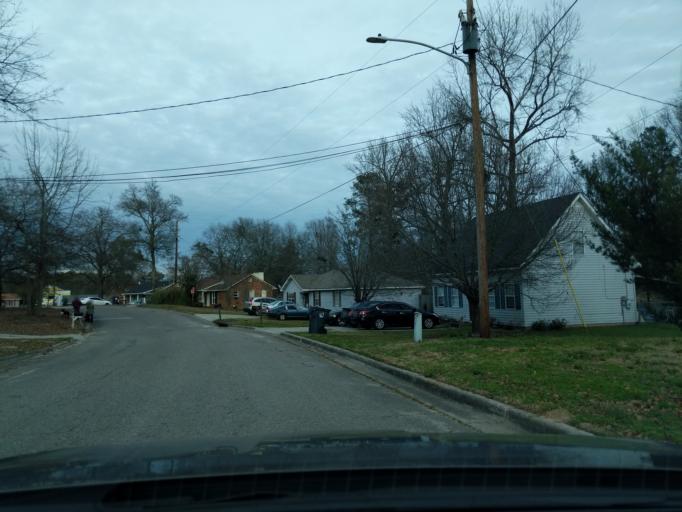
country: US
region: Georgia
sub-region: Columbia County
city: Grovetown
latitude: 33.4601
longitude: -82.1944
